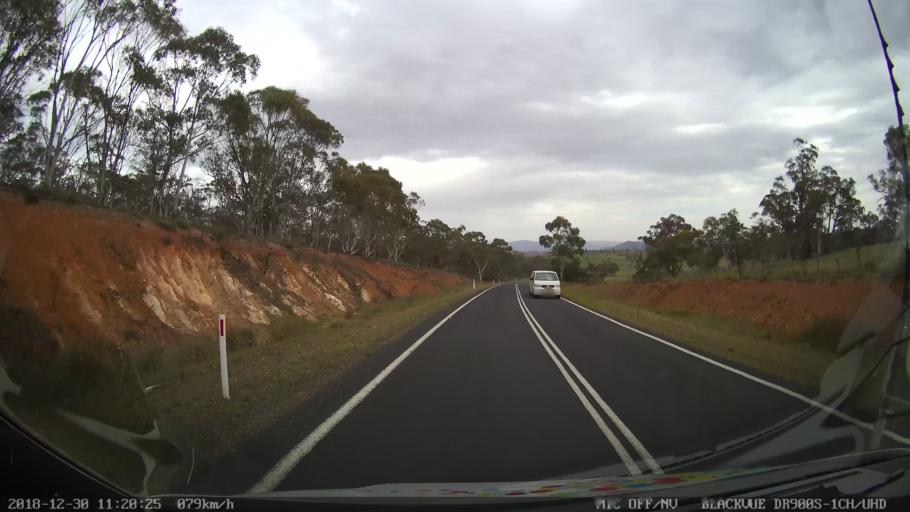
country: AU
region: New South Wales
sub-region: Snowy River
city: Jindabyne
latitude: -36.5185
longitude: 148.6890
